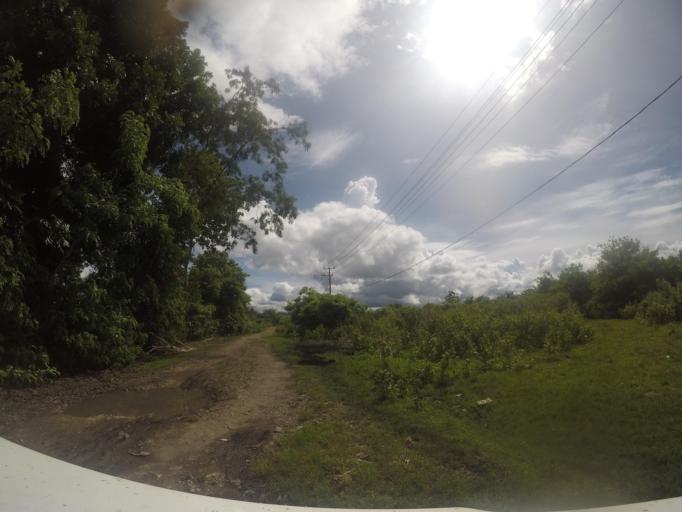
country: TL
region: Lautem
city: Lospalos
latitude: -8.4994
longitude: 127.0087
